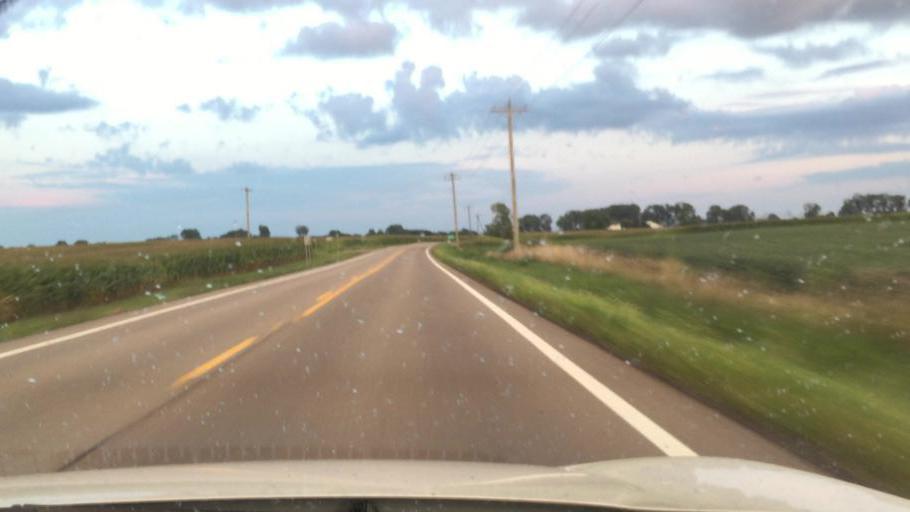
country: US
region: Ohio
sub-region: Champaign County
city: Mechanicsburg
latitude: 40.0444
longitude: -83.5132
